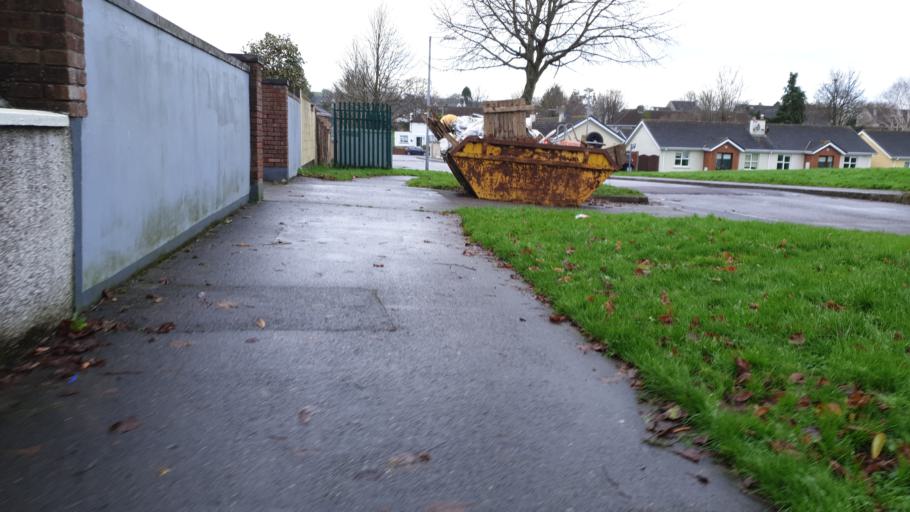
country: IE
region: Munster
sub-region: County Cork
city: Cork
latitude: 51.8960
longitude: -8.4086
